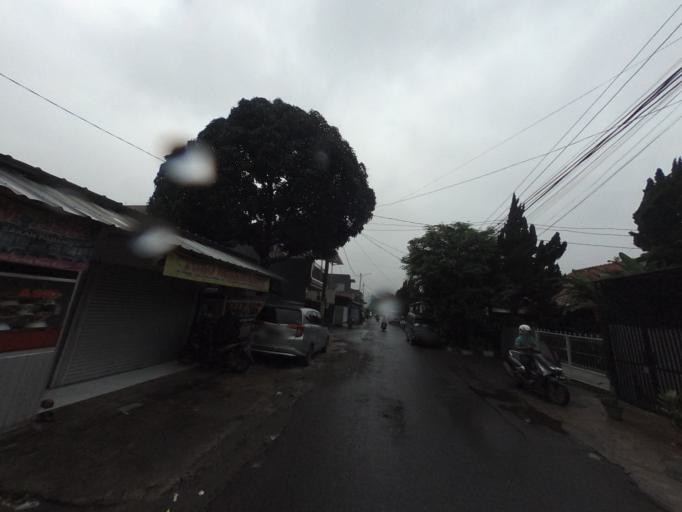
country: ID
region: West Java
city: Bogor
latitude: -6.5693
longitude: 106.7962
